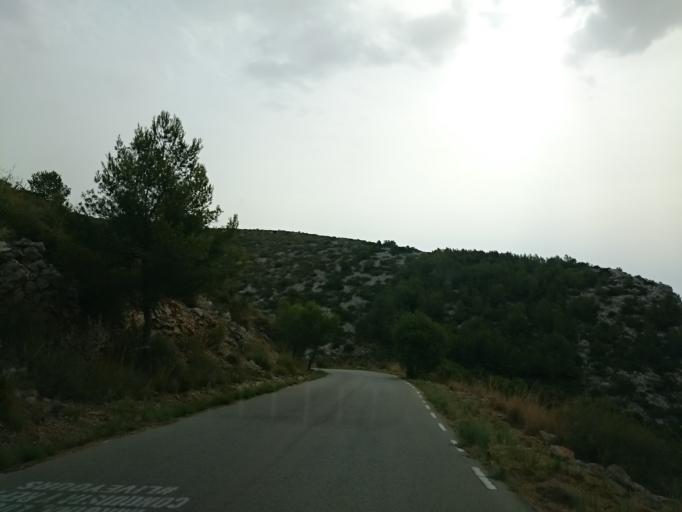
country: ES
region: Catalonia
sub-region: Provincia de Barcelona
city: Castelldefels
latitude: 41.2719
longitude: 1.9182
